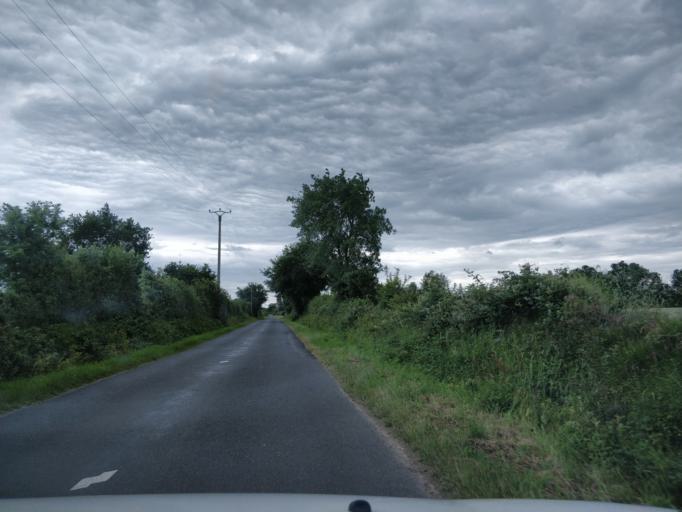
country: FR
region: Pays de la Loire
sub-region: Departement de Maine-et-Loire
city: Feneu
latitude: 47.6207
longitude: -0.6248
